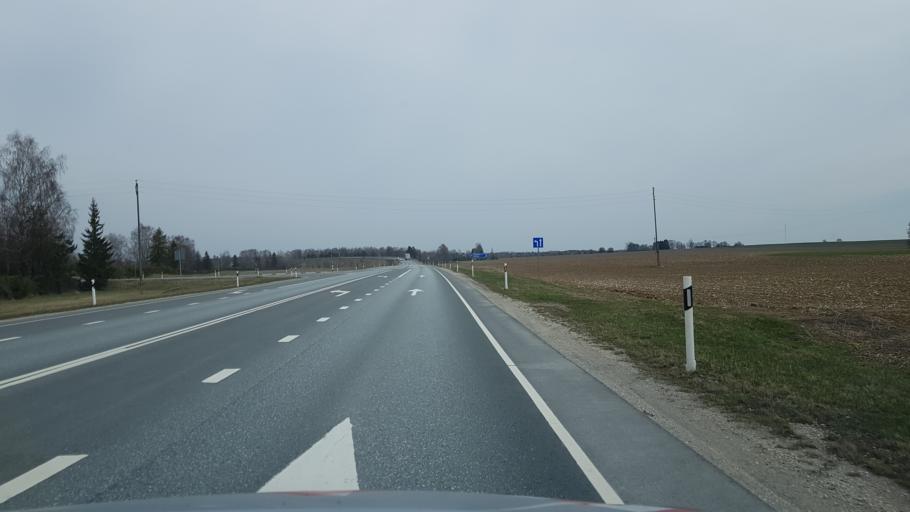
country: EE
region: Laeaene-Virumaa
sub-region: Kadrina vald
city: Kadrina
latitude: 59.3308
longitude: 26.1079
